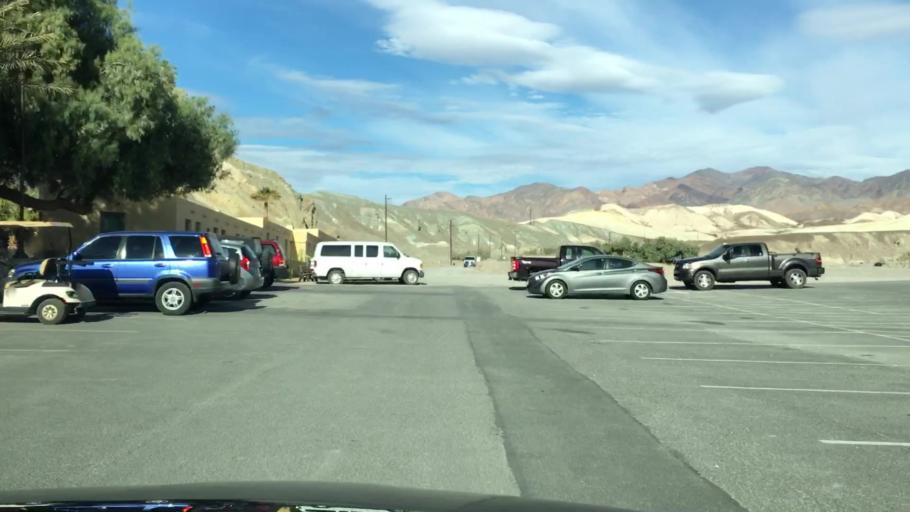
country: US
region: Nevada
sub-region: Nye County
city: Beatty
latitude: 36.4504
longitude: -116.8514
